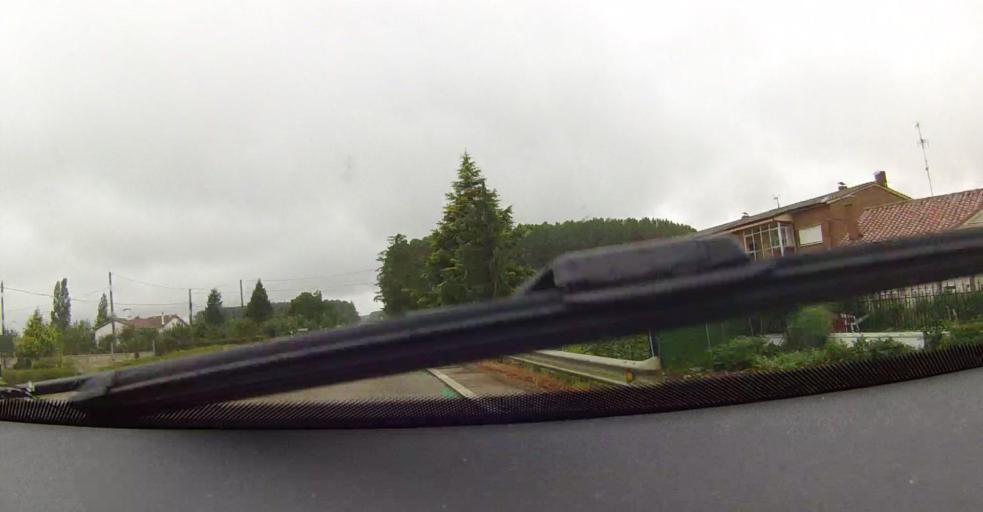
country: ES
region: Castille and Leon
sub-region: Provincia de Palencia
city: Saldana
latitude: 42.4997
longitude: -4.7301
